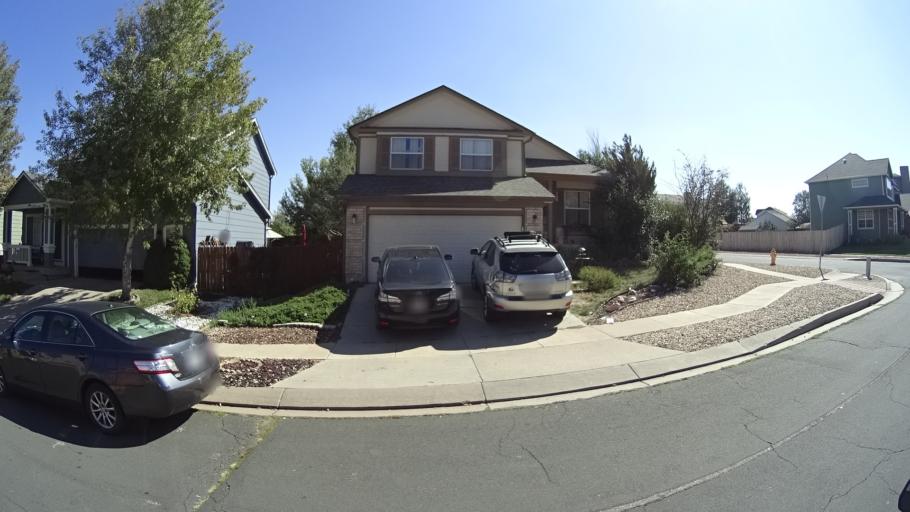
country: US
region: Colorado
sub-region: El Paso County
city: Cimarron Hills
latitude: 38.8827
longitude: -104.6998
